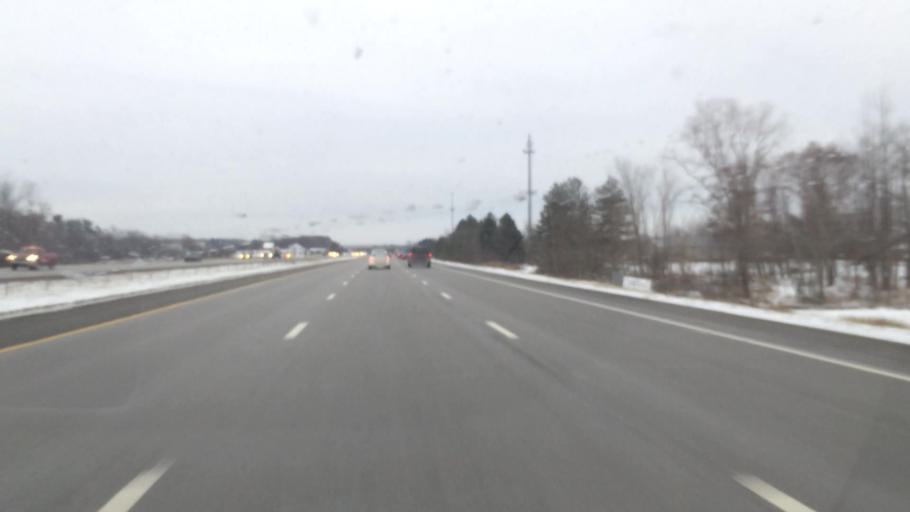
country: US
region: Ohio
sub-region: Medina County
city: Brunswick
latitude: 41.2690
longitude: -81.8054
